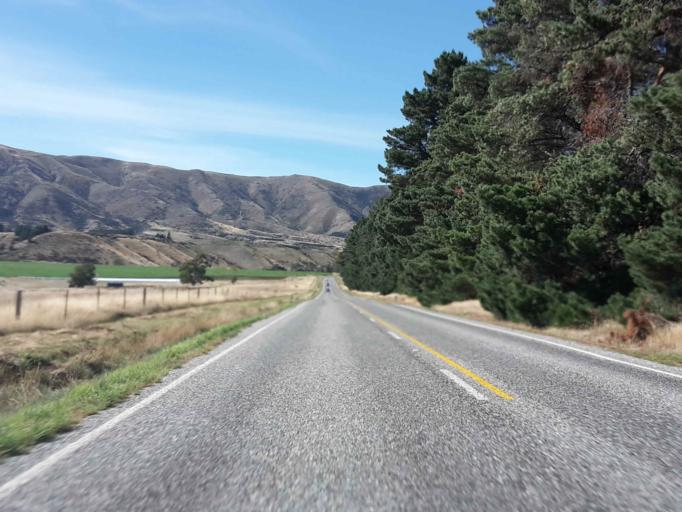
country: NZ
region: Otago
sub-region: Queenstown-Lakes District
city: Wanaka
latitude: -44.7334
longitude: 169.3041
